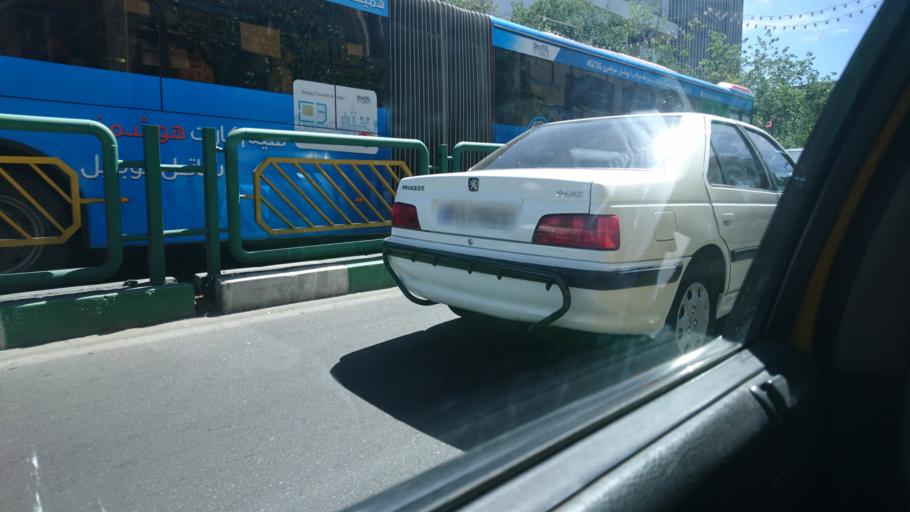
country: IR
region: Tehran
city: Tehran
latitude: 35.7013
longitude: 51.4002
